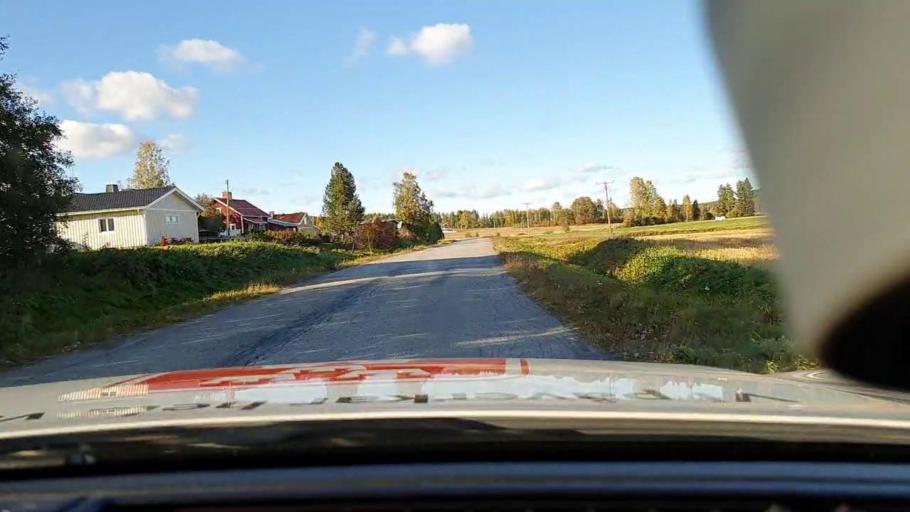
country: SE
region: Norrbotten
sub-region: Pitea Kommun
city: Norrfjarden
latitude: 65.5220
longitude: 21.4926
